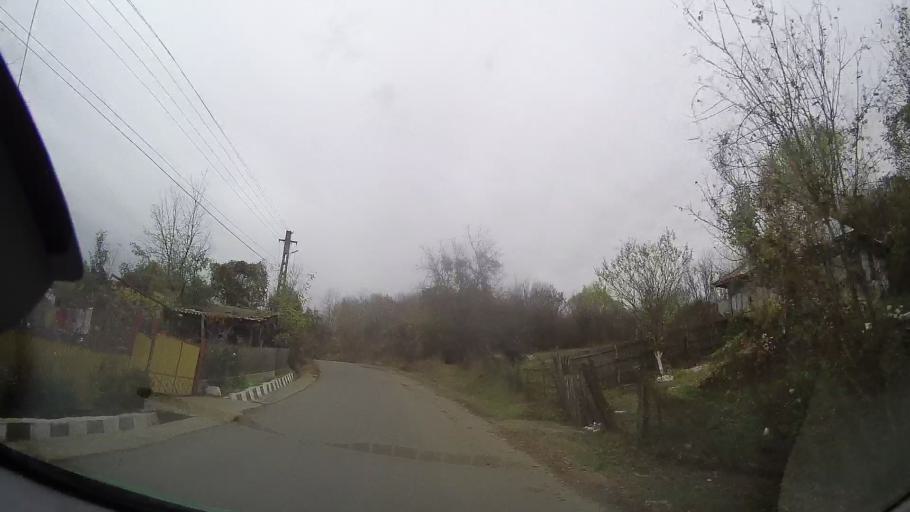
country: RO
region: Prahova
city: Mocesti
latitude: 45.0634
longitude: 26.2604
